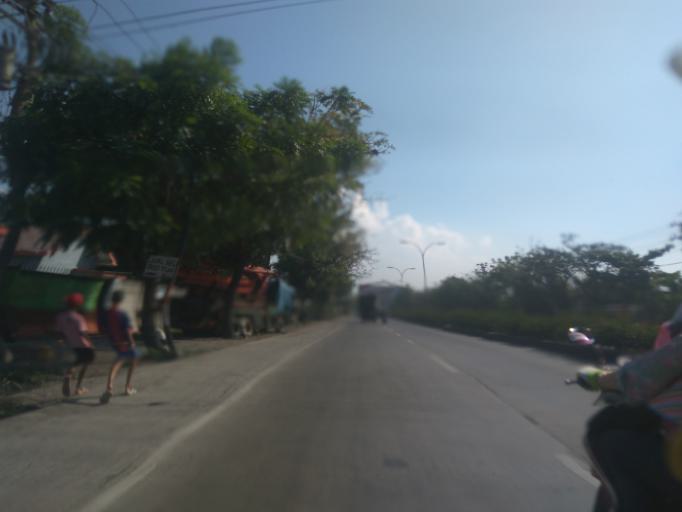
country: ID
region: Central Java
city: Mranggen
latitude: -6.9472
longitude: 110.4922
